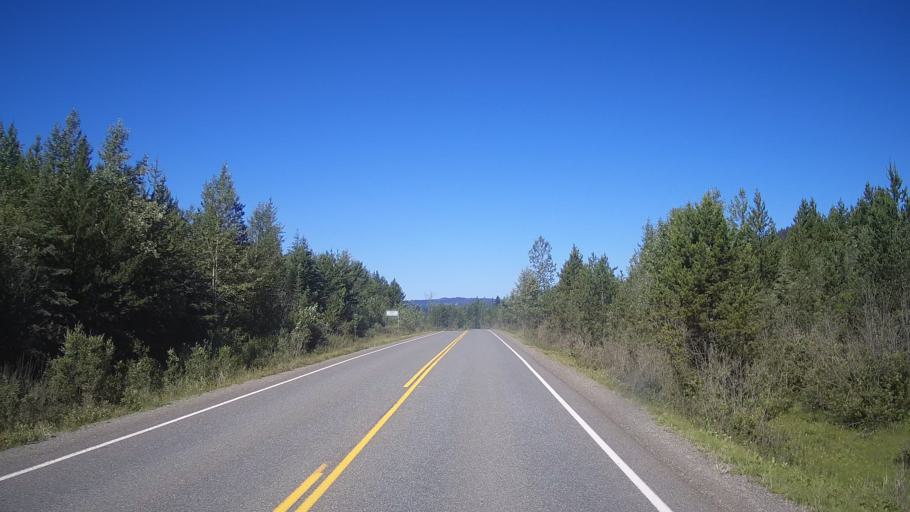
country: CA
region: British Columbia
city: Kamloops
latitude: 51.4962
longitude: -120.3999
